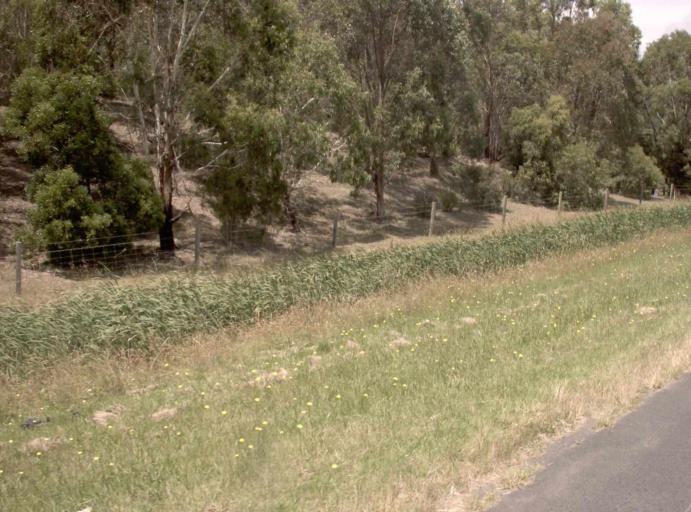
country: AU
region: Victoria
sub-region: Latrobe
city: Traralgon
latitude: -38.2229
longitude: 146.5447
